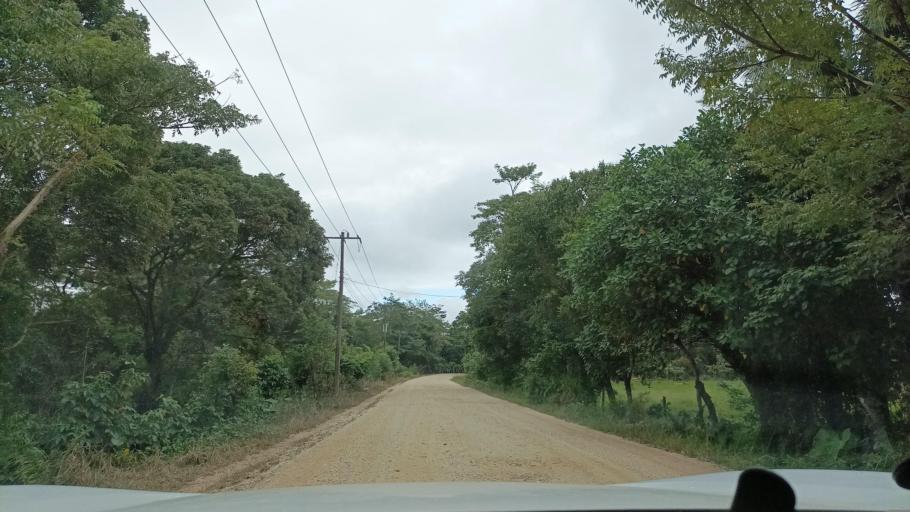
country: MX
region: Veracruz
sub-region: Moloacan
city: Cuichapa
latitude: 17.8490
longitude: -94.3615
